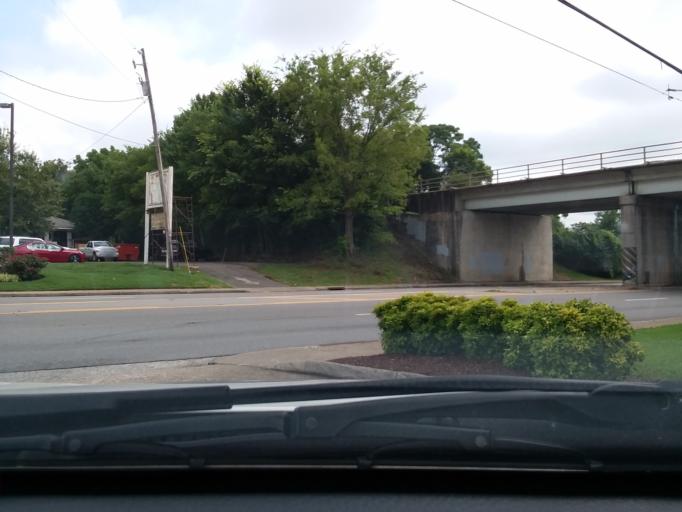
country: US
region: Tennessee
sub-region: Davidson County
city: Goodlettsville
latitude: 36.3226
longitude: -86.7092
